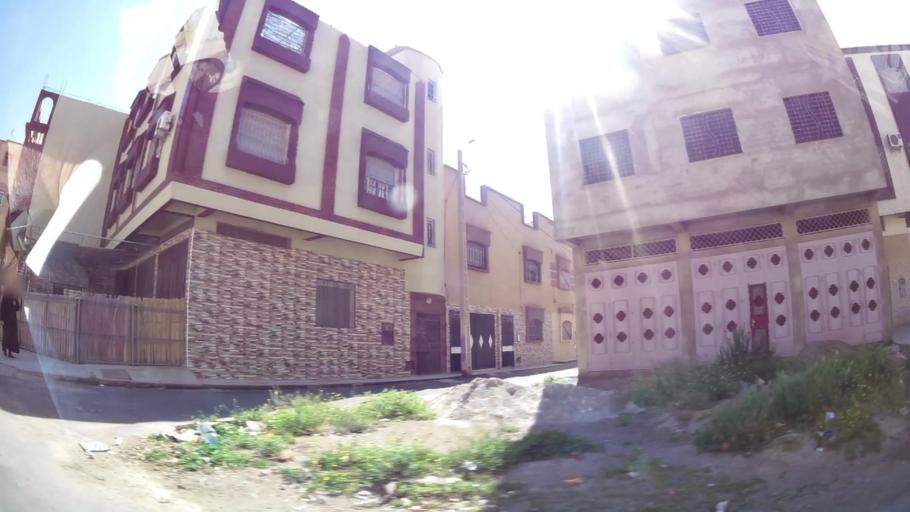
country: MA
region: Oriental
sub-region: Oujda-Angad
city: Oujda
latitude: 34.6763
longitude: -1.9345
